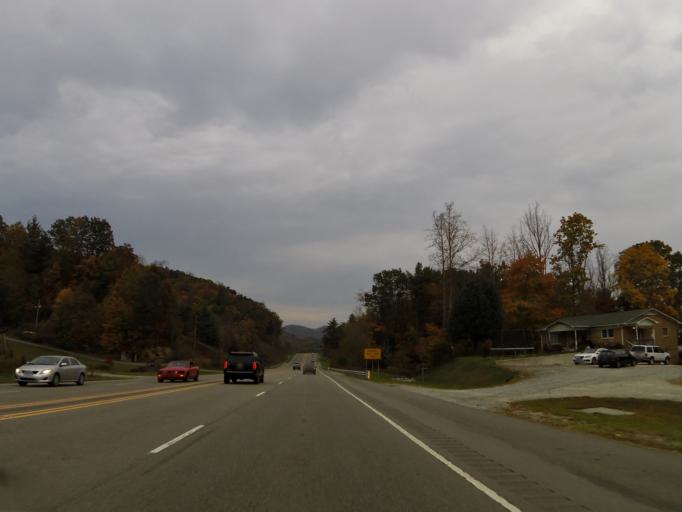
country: US
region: North Carolina
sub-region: Watauga County
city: Blowing Rock
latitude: 36.0610
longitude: -81.6046
